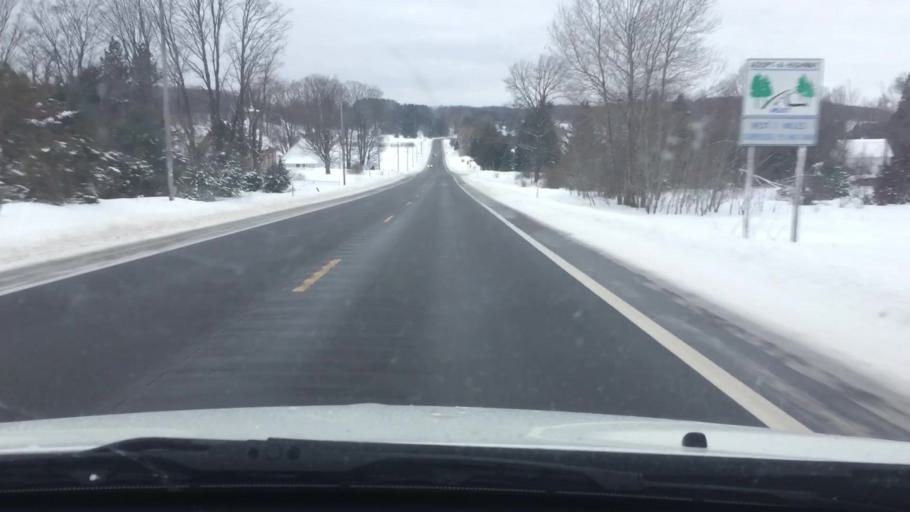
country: US
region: Michigan
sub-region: Charlevoix County
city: East Jordan
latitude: 45.1035
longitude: -85.0379
